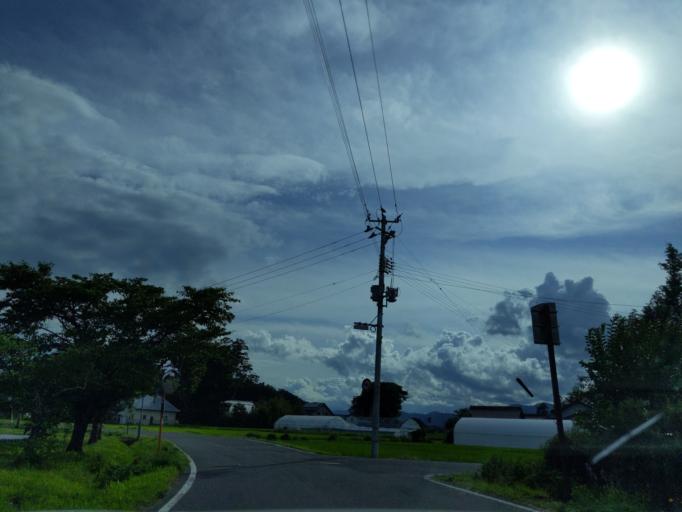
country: JP
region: Fukushima
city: Koriyama
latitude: 37.3458
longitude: 140.3047
